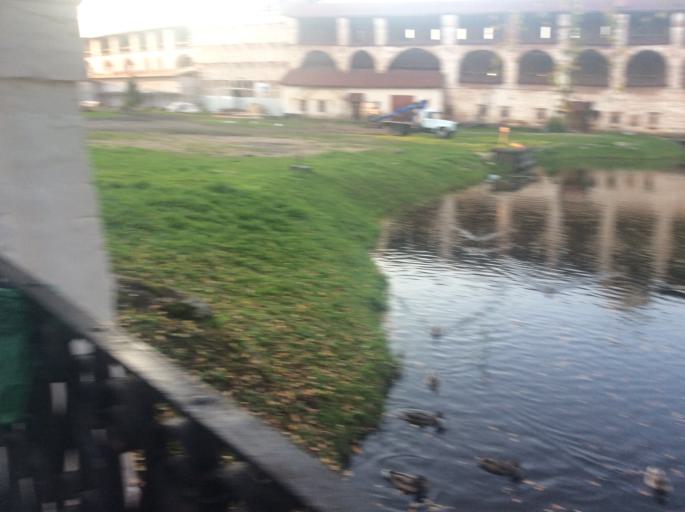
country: RU
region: Vologda
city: Kirillov
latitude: 59.8581
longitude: 38.3686
